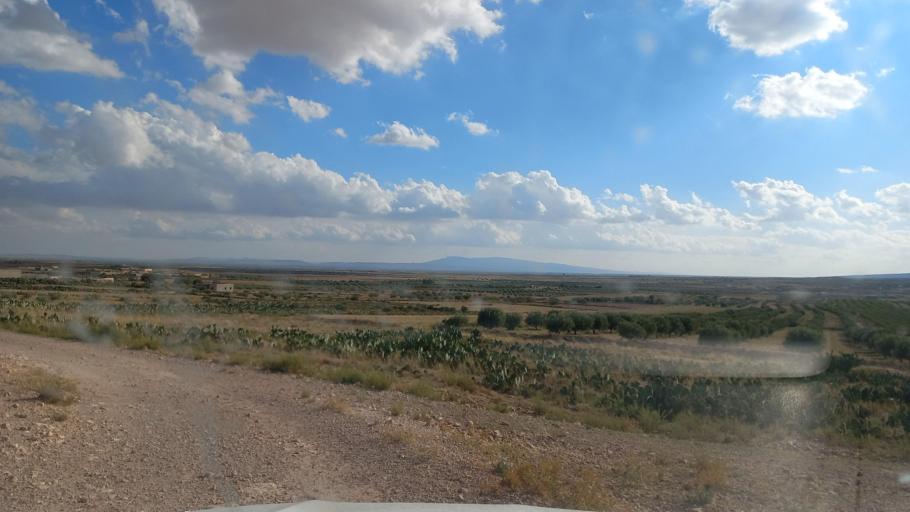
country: TN
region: Al Qasrayn
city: Sbiba
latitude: 35.3933
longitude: 9.0405
